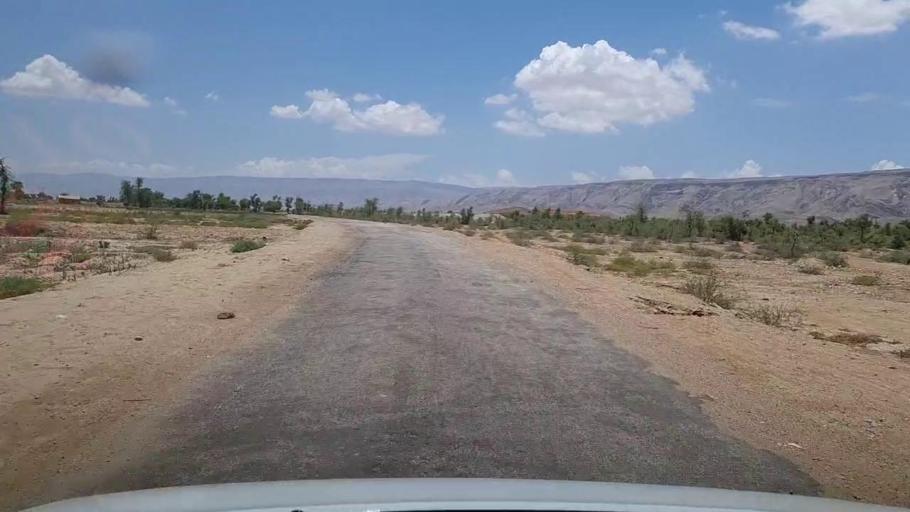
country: PK
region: Sindh
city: Bhan
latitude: 26.2701
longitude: 67.5222
